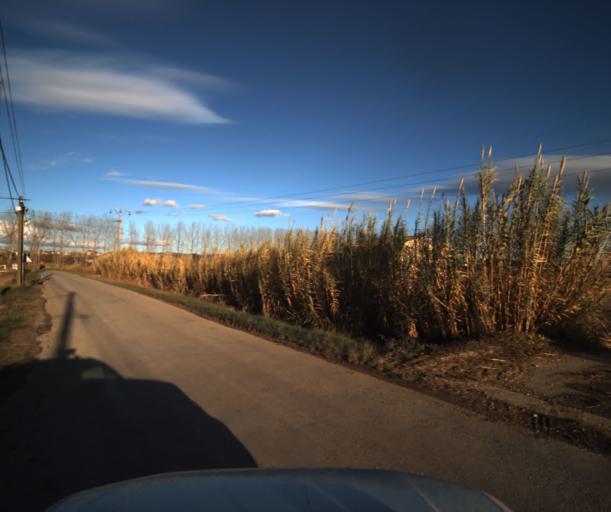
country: FR
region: Provence-Alpes-Cote d'Azur
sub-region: Departement du Vaucluse
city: Pertuis
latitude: 43.6810
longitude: 5.4924
